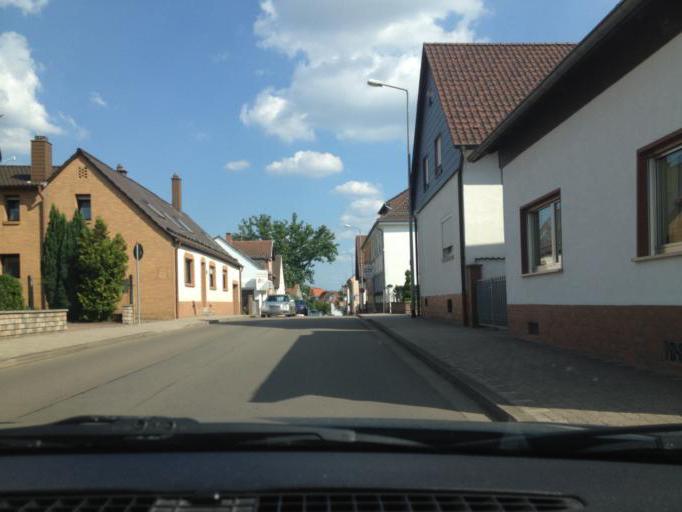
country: DE
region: Rheinland-Pfalz
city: Ramstein-Miesenbach
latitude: 49.4484
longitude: 7.5505
